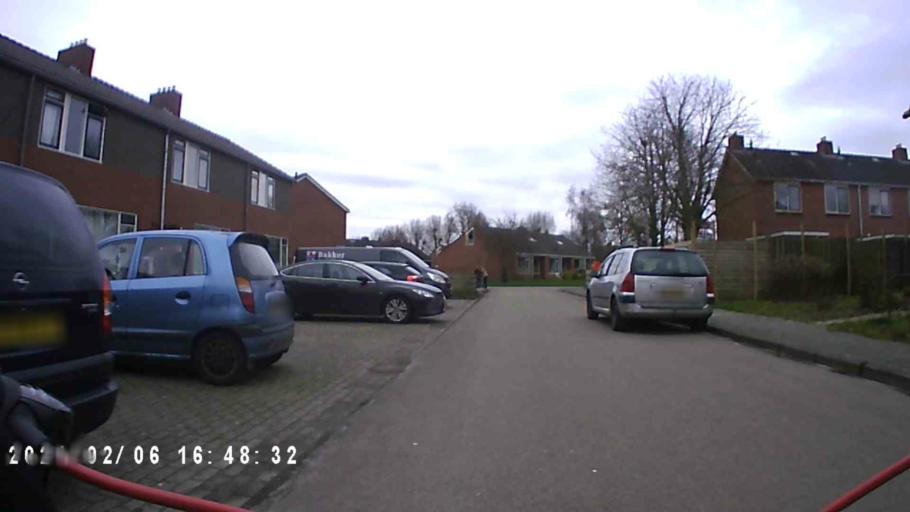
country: NL
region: Groningen
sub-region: Gemeente Appingedam
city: Appingedam
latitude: 53.4148
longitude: 6.7324
